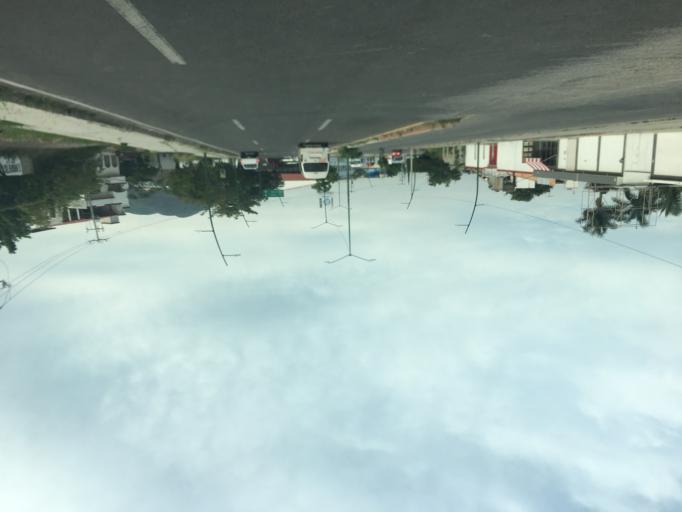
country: MX
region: Chiapas
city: Tuxtla Gutierrez
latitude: 16.7652
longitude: -93.1627
